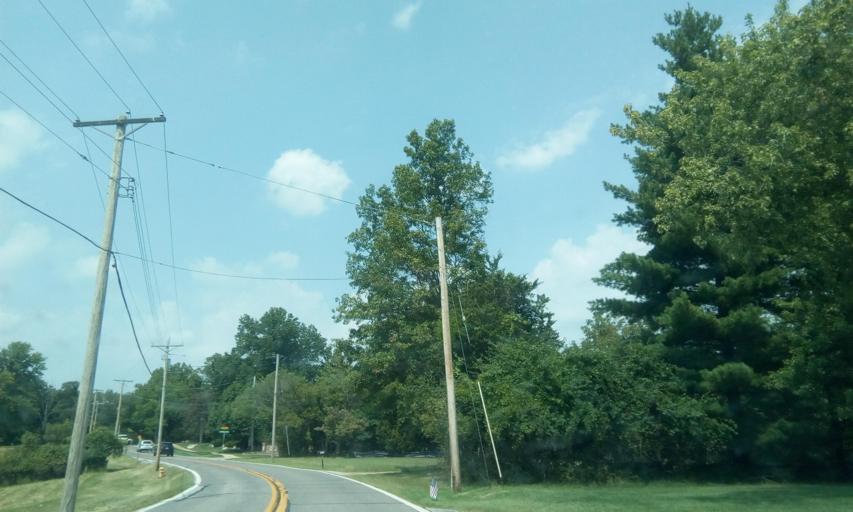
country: US
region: Missouri
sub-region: Saint Louis County
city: Town and Country
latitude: 38.6033
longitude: -90.4822
